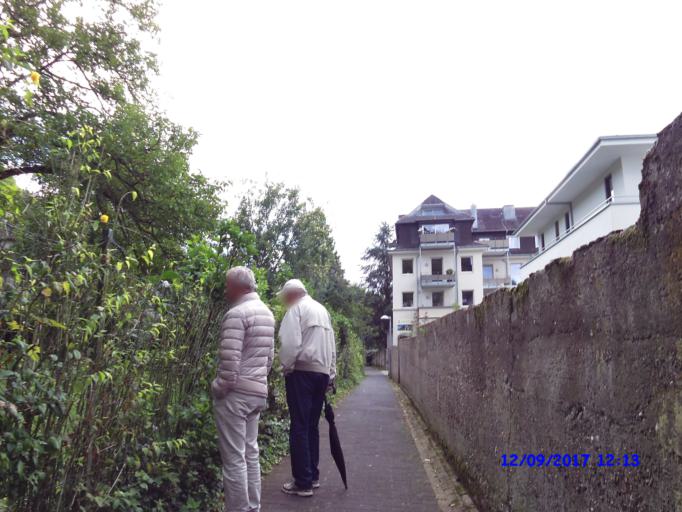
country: DE
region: North Rhine-Westphalia
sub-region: Regierungsbezirk Koln
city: Bad Honnef
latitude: 50.6594
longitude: 7.2144
